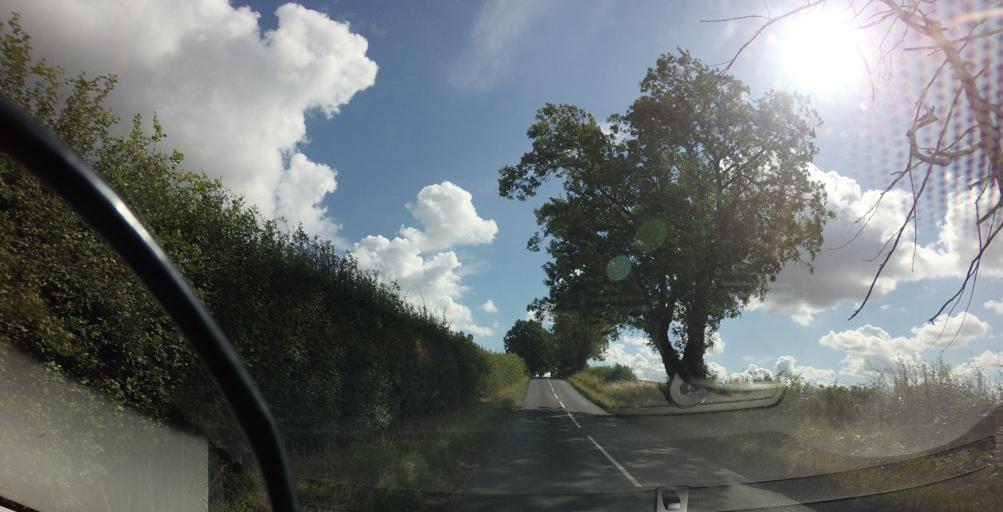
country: GB
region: England
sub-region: North Yorkshire
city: Boroughbridge
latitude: 54.0481
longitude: -1.3950
